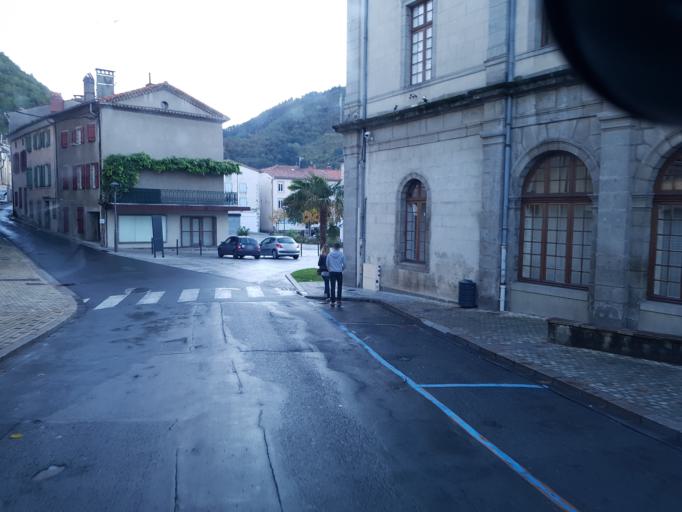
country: FR
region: Midi-Pyrenees
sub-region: Departement du Tarn
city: Mazamet
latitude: 43.4907
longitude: 2.3771
